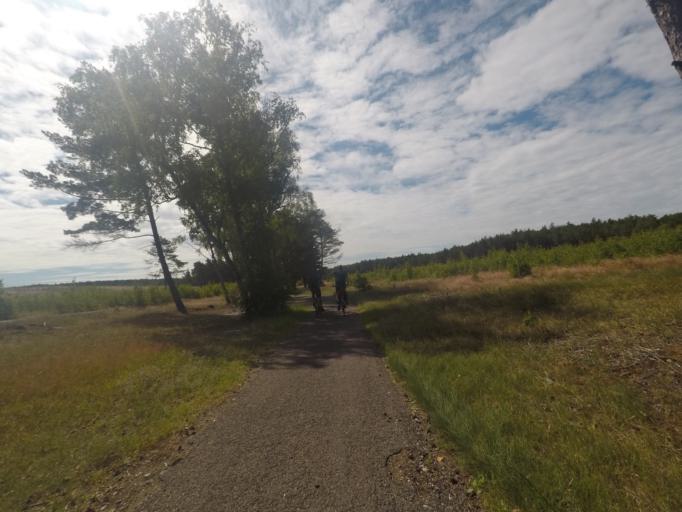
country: LT
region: Klaipedos apskritis
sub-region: Klaipeda
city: Klaipeda
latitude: 55.5876
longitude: 21.1128
